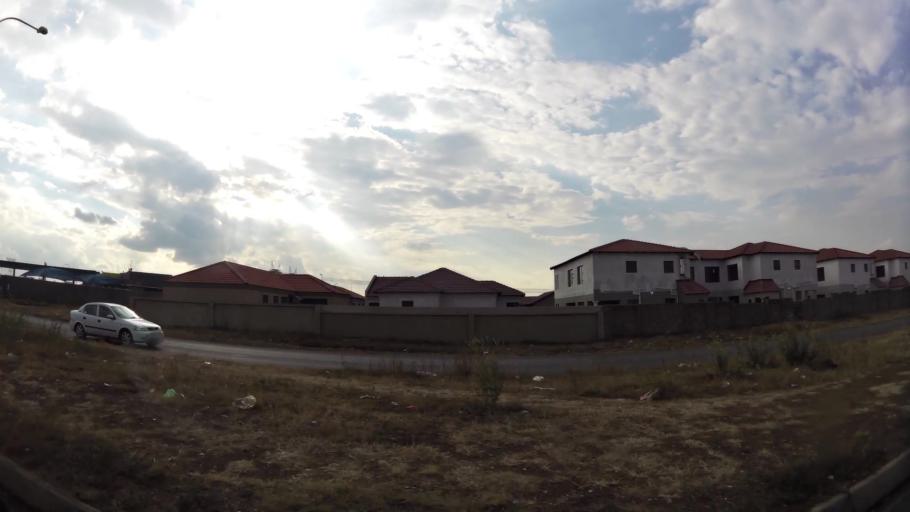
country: ZA
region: Gauteng
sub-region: Sedibeng District Municipality
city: Vanderbijlpark
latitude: -26.6990
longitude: 27.8797
